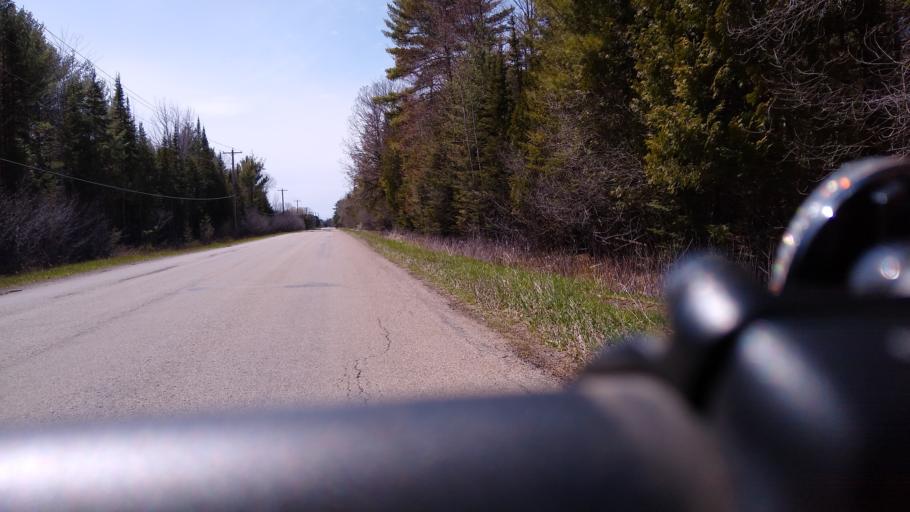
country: US
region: Michigan
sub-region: Delta County
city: Escanaba
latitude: 45.7353
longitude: -87.1767
